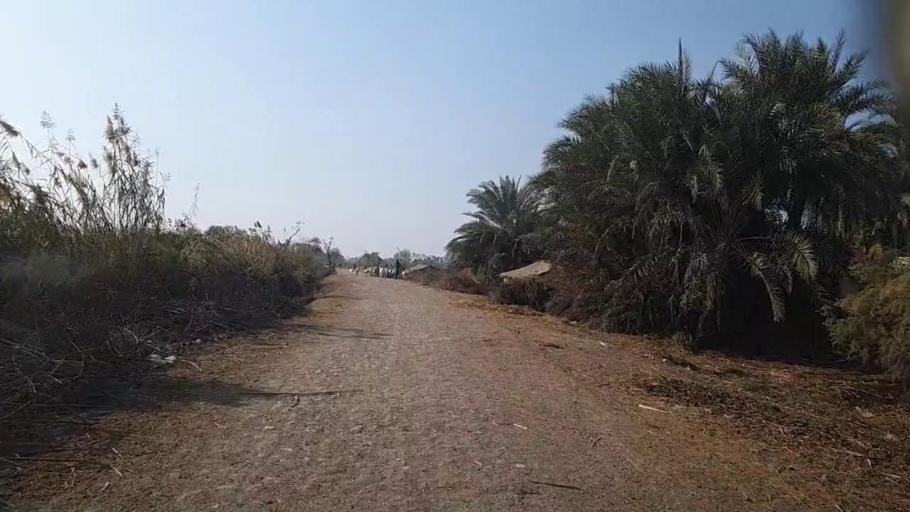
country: PK
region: Sindh
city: Mirpur Mathelo
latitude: 27.9036
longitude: 69.6170
